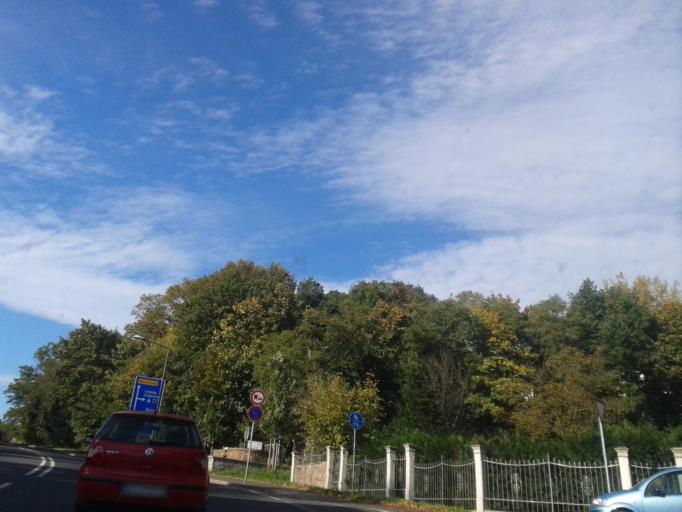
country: DE
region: Saxony
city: Albertstadt
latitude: 51.0975
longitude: 13.7186
